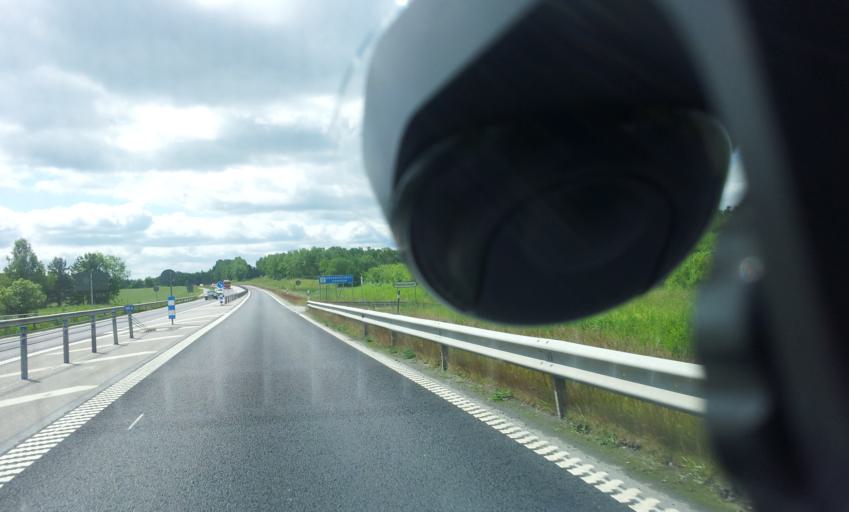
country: SE
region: OEstergoetland
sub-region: Soderkopings Kommun
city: Soederkoeping
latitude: 58.5159
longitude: 16.2884
